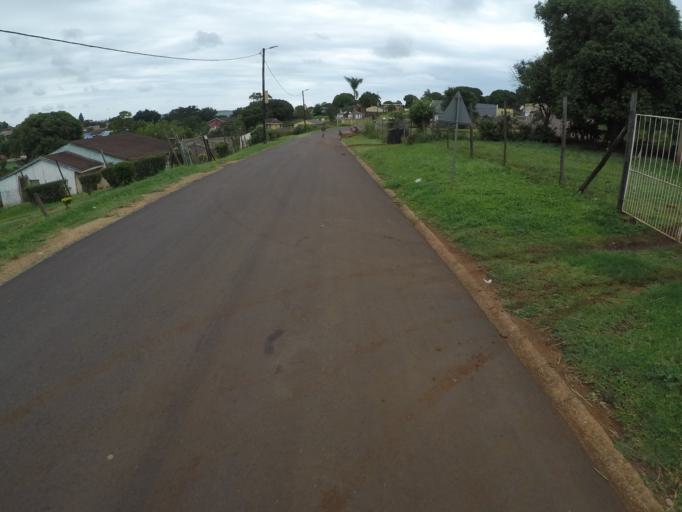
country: ZA
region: KwaZulu-Natal
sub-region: uThungulu District Municipality
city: Empangeni
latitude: -28.7684
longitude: 31.8654
